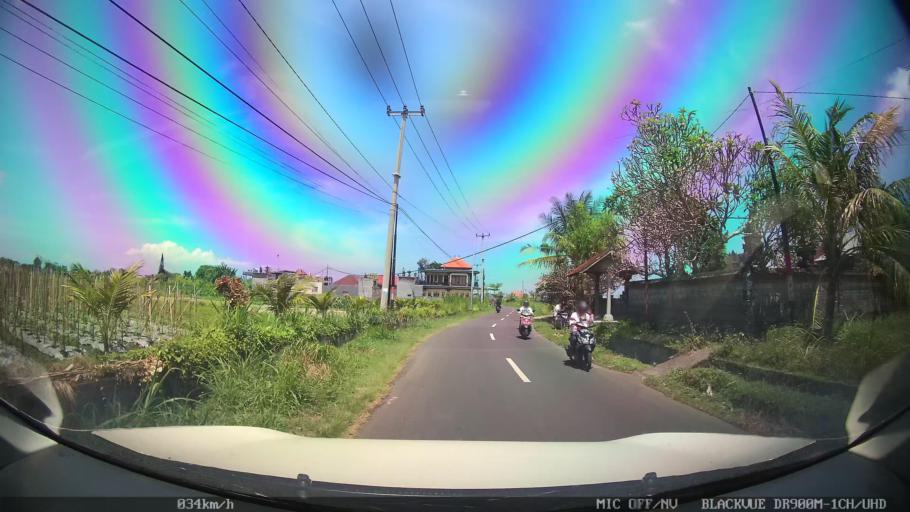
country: ID
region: Bali
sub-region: Kabupaten Gianyar
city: Ubud
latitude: -8.5624
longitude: 115.3194
